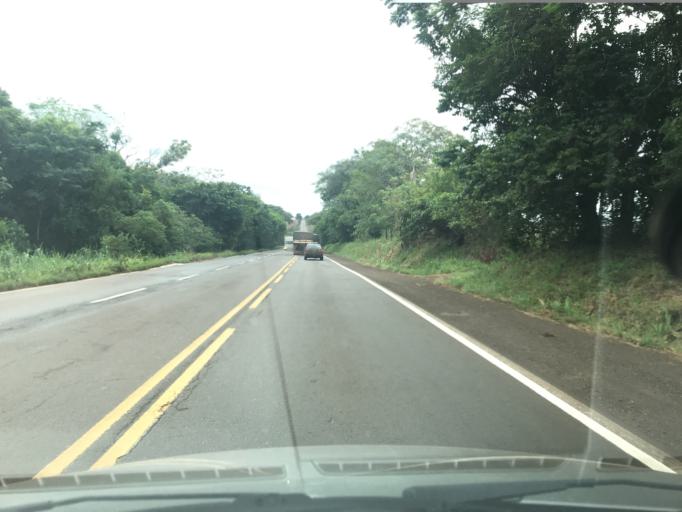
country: BR
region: Parana
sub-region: Terra Boa
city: Terra Boa
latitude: -23.6189
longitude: -52.4362
